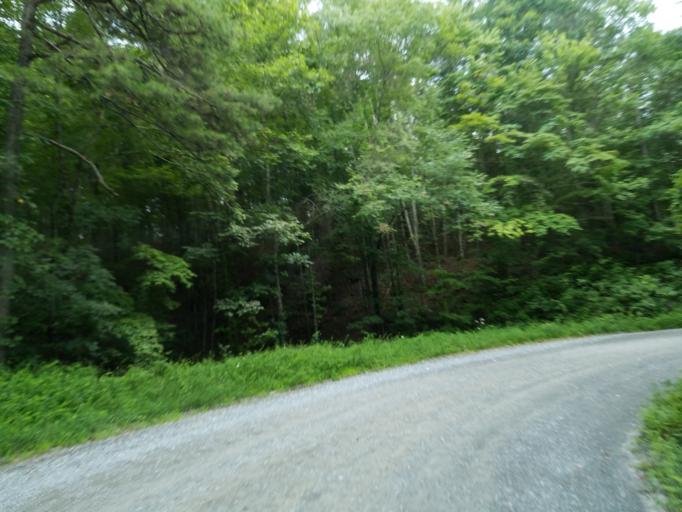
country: US
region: Georgia
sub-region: Fannin County
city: Blue Ridge
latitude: 34.8275
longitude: -84.2293
